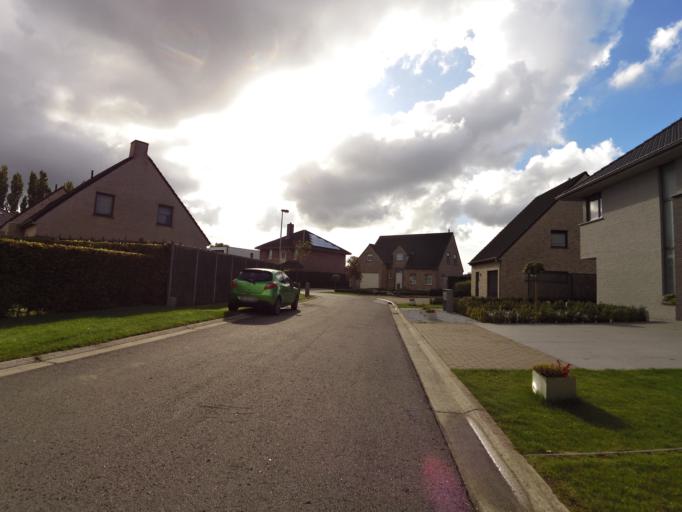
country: BE
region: Flanders
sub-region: Provincie West-Vlaanderen
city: Middelkerke
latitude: 51.1724
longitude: 2.8724
